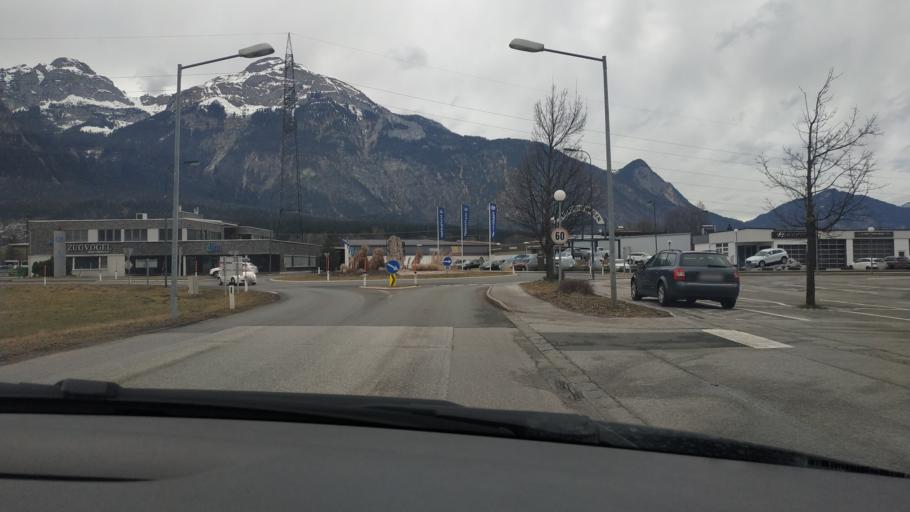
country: AT
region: Tyrol
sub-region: Politischer Bezirk Schwaz
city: Strass im Zillertal
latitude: 47.3971
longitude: 11.8177
